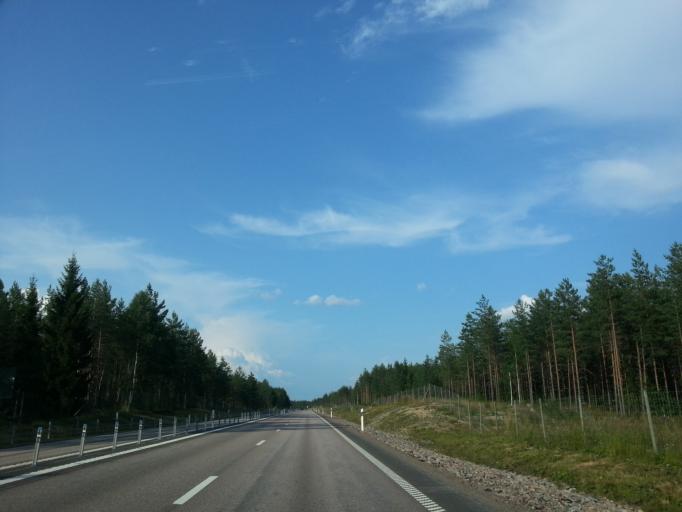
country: SE
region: Vaestmanland
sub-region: Norbergs Kommun
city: Norberg
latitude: 60.0769
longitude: 15.9736
